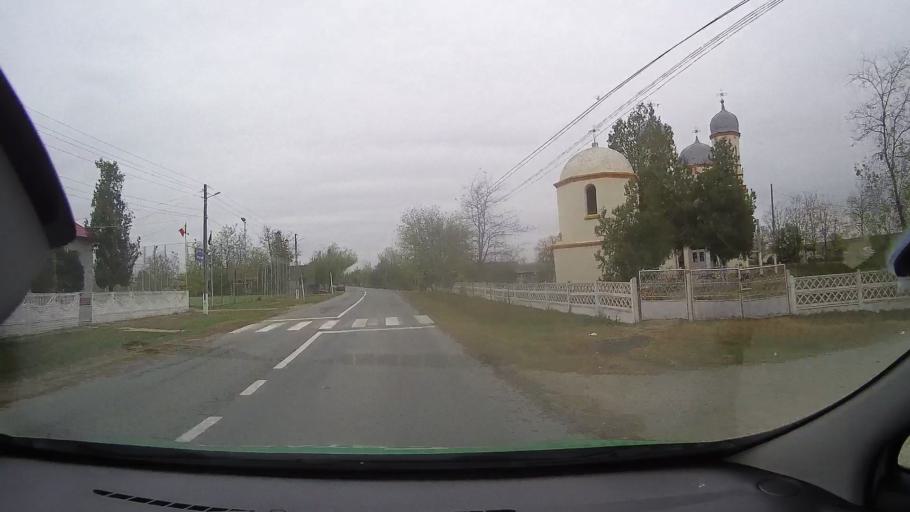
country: RO
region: Constanta
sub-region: Comuna Silistea
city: Silistea
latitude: 44.4461
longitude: 28.2385
